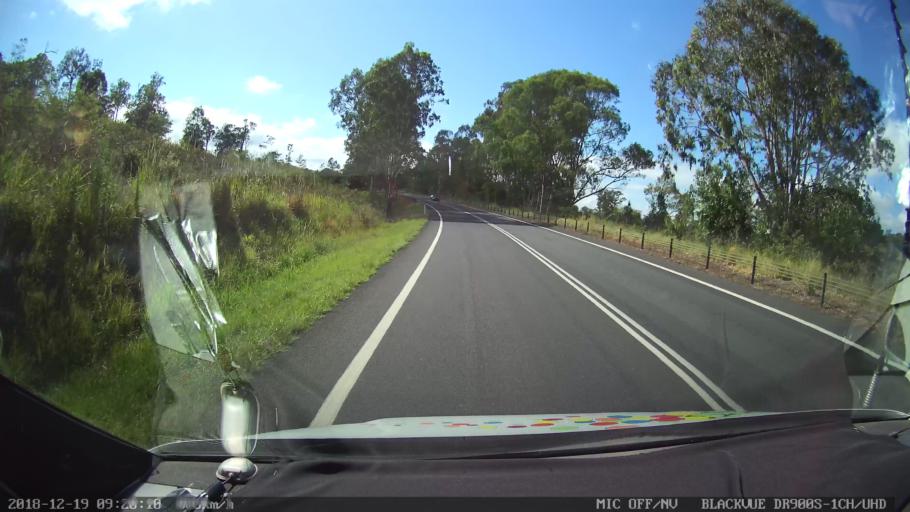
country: AU
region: New South Wales
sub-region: Kyogle
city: Kyogle
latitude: -28.5693
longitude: 152.9782
